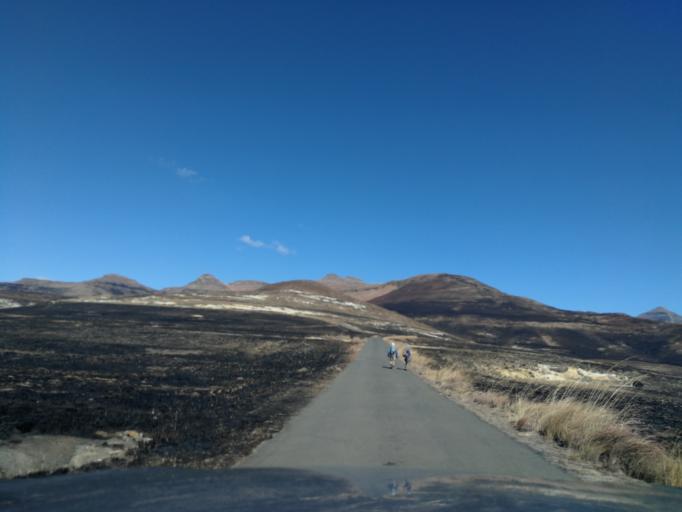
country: ZA
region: Orange Free State
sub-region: Thabo Mofutsanyana District Municipality
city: Phuthaditjhaba
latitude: -28.5168
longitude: 28.6224
